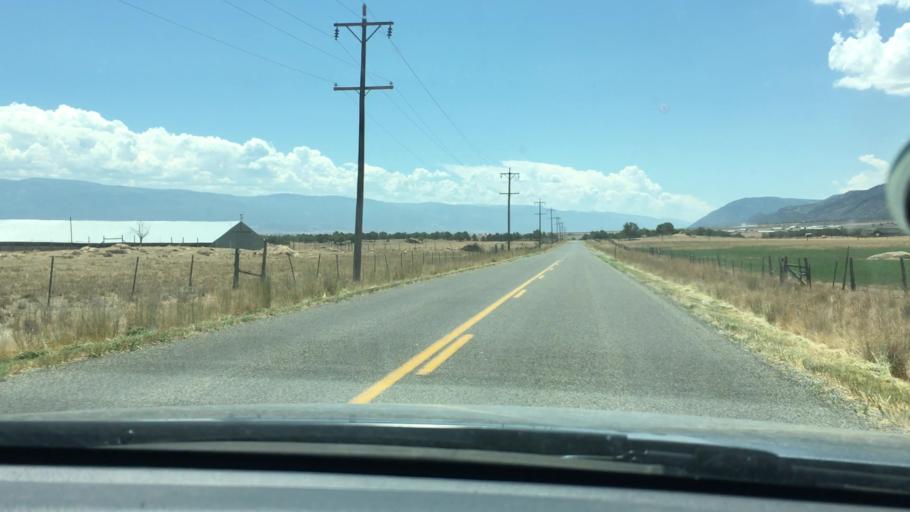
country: US
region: Utah
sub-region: Sanpete County
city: Fountain Green
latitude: 39.5973
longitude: -111.6433
